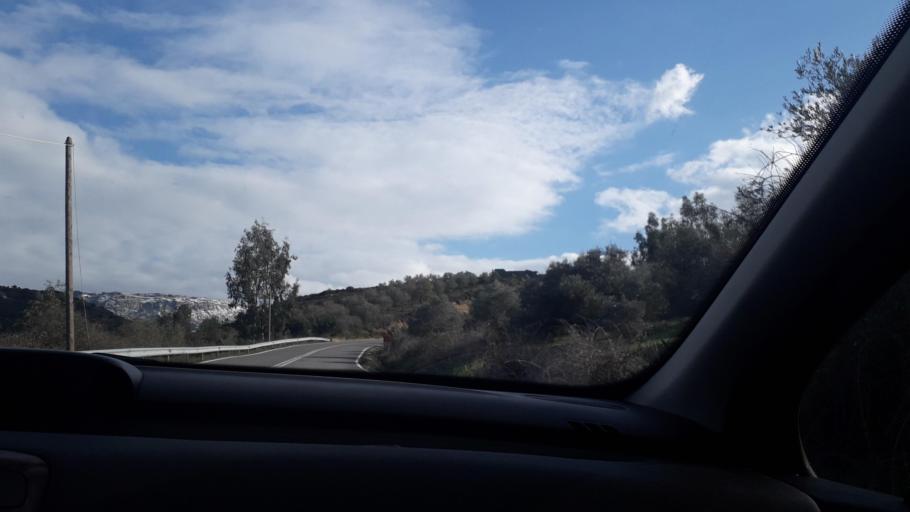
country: GR
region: Crete
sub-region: Nomos Rethymnis
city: Agia Foteini
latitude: 35.2880
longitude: 24.5633
